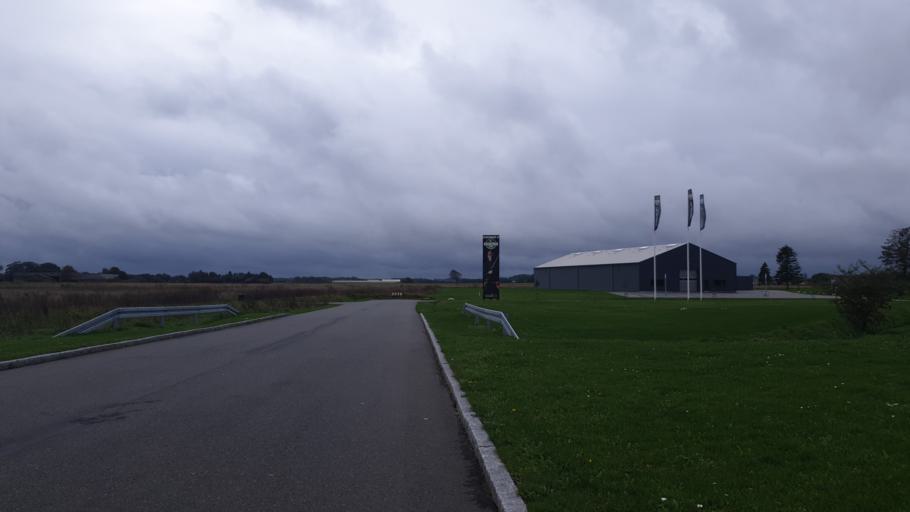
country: DK
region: Central Jutland
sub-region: Hedensted Kommune
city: Hedensted
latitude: 55.7820
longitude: 9.6653
